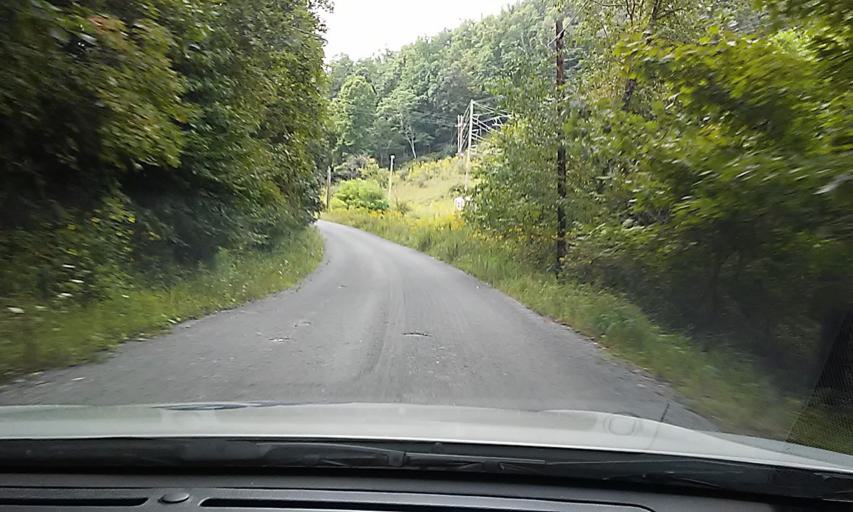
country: US
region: West Virginia
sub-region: Marion County
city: Mannington
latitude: 39.6321
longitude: -80.3580
